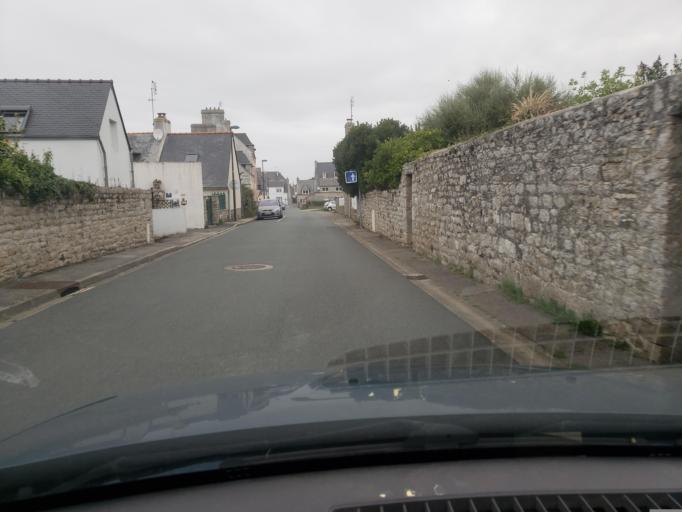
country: FR
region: Brittany
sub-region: Departement du Finistere
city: Guilvinec
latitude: 47.8003
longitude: -4.3571
